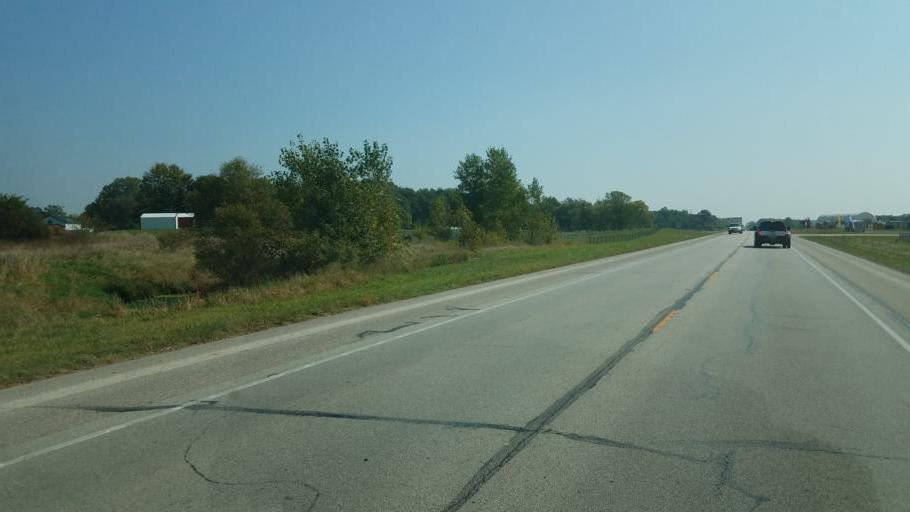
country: US
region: Indiana
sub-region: LaGrange County
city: Topeka
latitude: 41.6488
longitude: -85.5638
